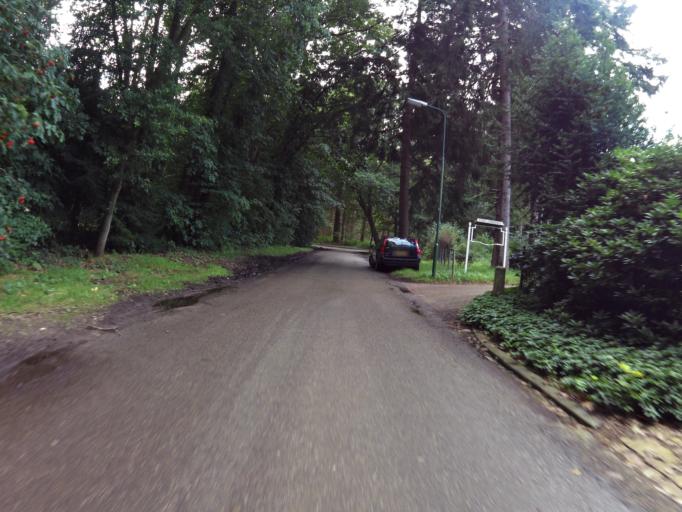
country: NL
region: Utrecht
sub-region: Gemeente Soest
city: Soest
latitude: 52.1578
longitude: 5.2832
